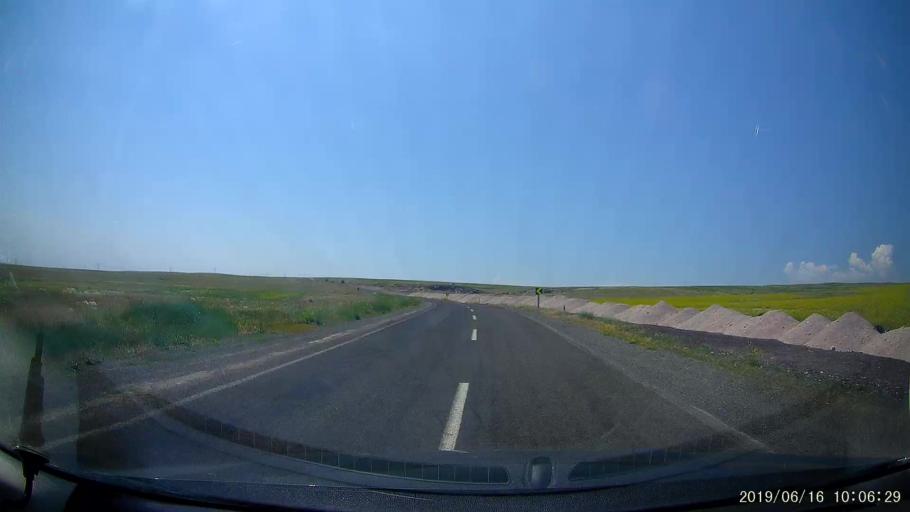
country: TR
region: Kars
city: Digor
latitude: 40.2548
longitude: 43.5426
